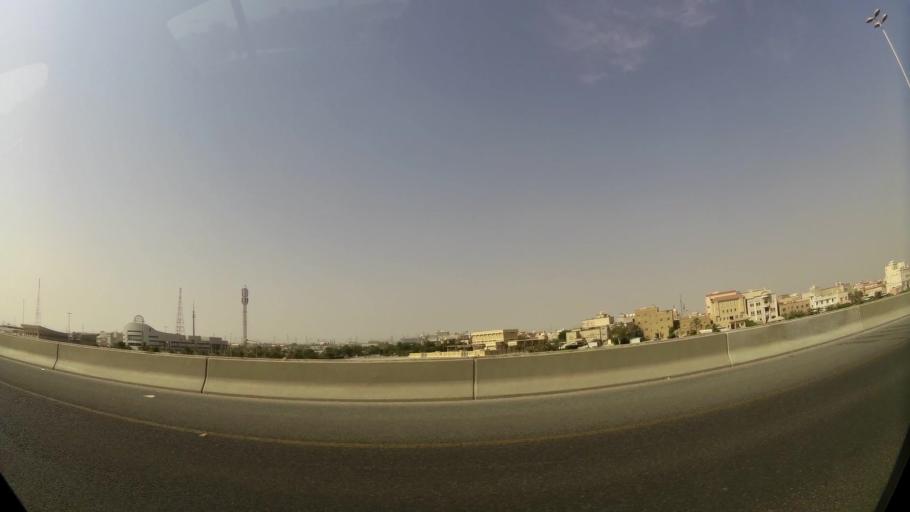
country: KW
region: Al Ahmadi
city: Al Manqaf
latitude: 29.0922
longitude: 48.1161
